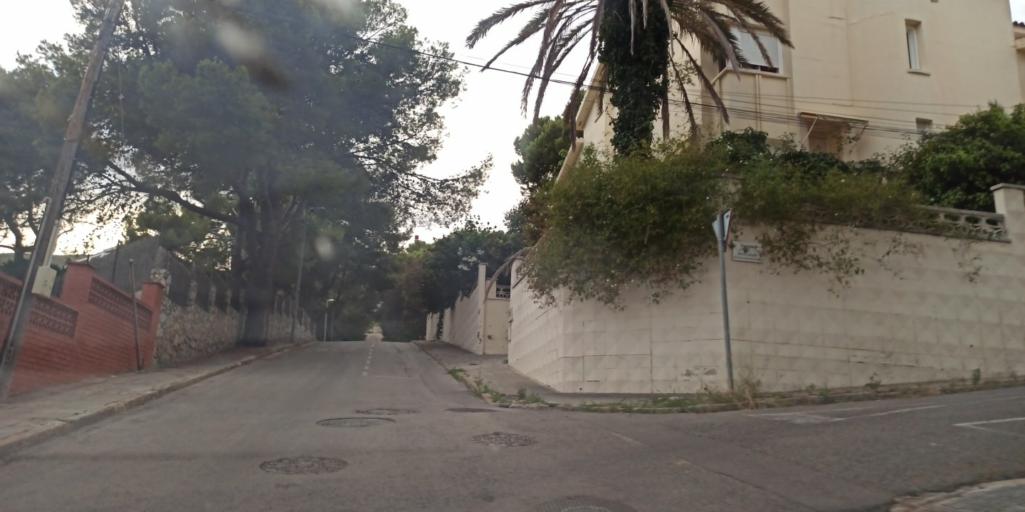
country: ES
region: Catalonia
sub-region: Provincia de Barcelona
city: Castelldefels
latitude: 41.2817
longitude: 1.9652
